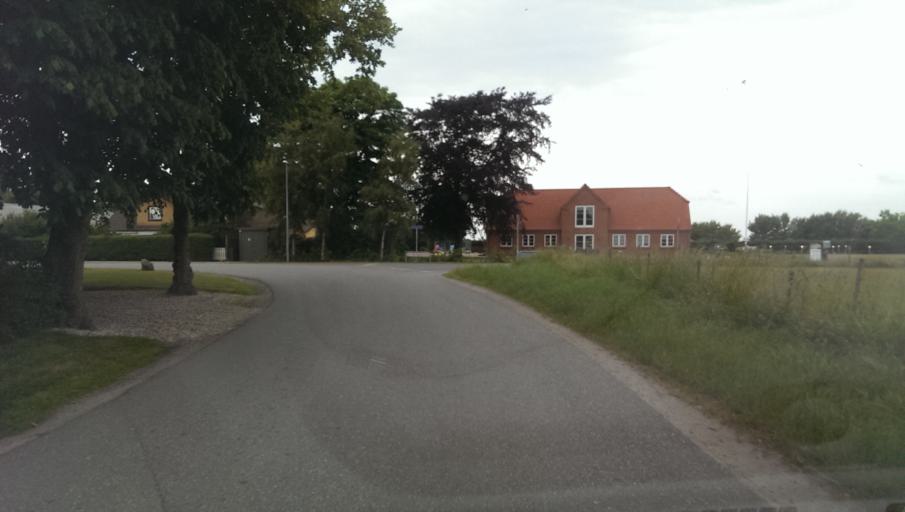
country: DK
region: South Denmark
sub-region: Esbjerg Kommune
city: Bramming
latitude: 55.4445
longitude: 8.6489
